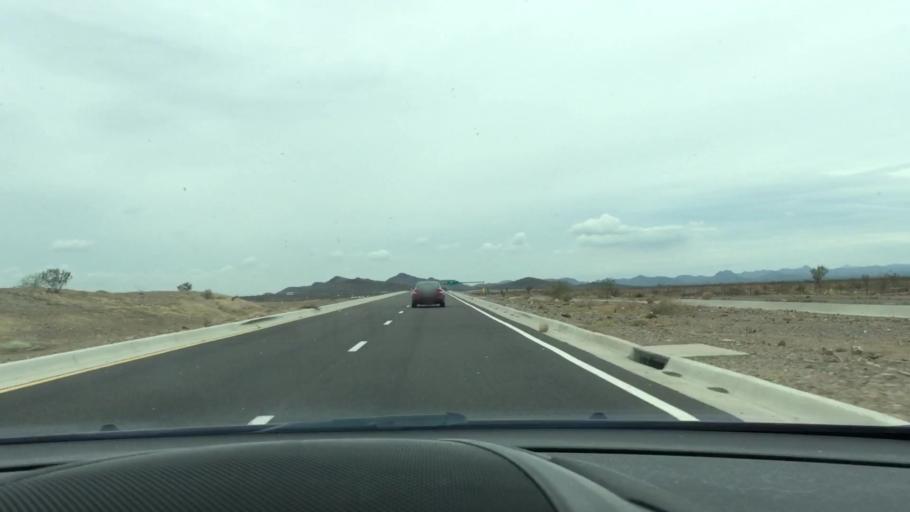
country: US
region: Arizona
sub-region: Maricopa County
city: Anthem
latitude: 33.7695
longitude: -112.1458
